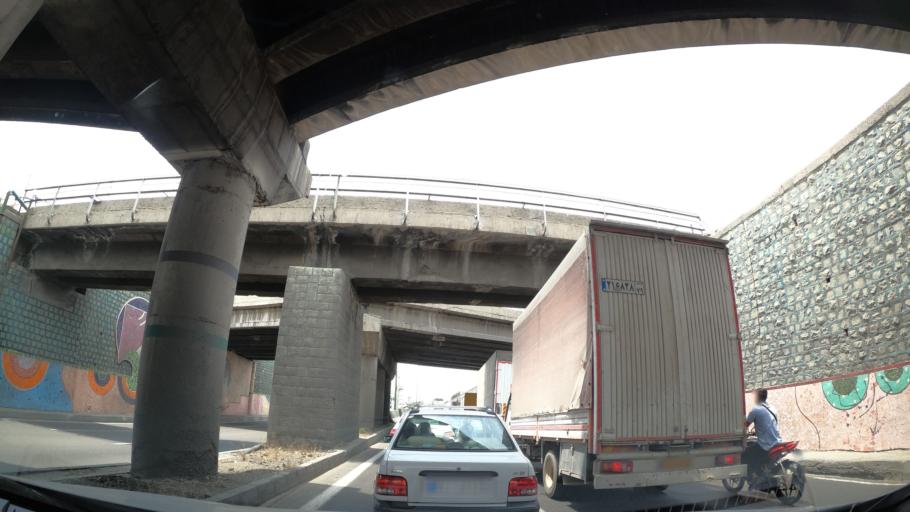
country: IR
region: Tehran
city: Shahr-e Qods
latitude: 35.6919
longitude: 51.2121
